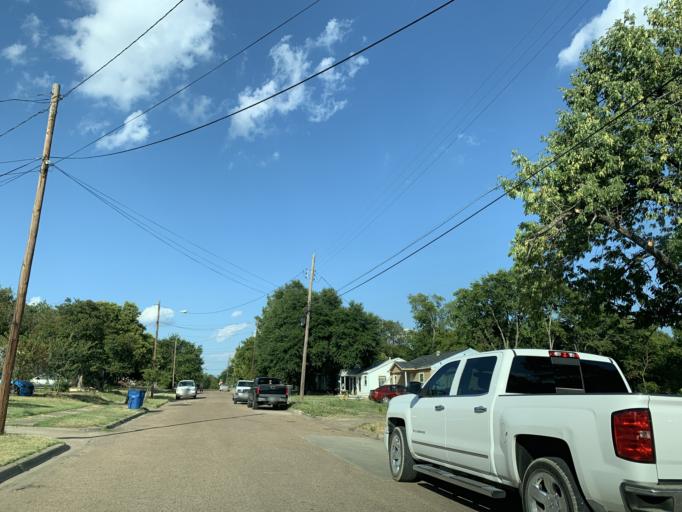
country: US
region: Texas
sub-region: Dallas County
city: Hutchins
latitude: 32.6947
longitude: -96.7812
